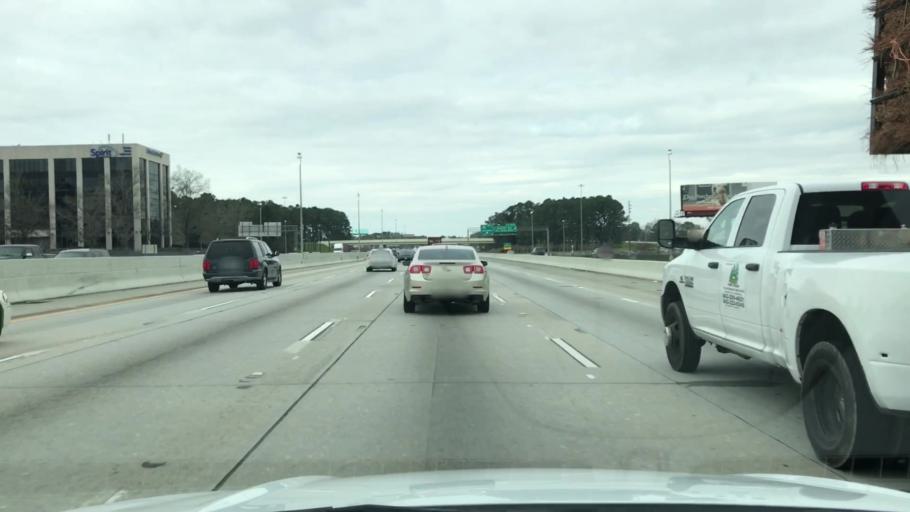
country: US
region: South Carolina
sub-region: Berkeley County
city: Hanahan
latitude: 32.8995
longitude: -80.0210
